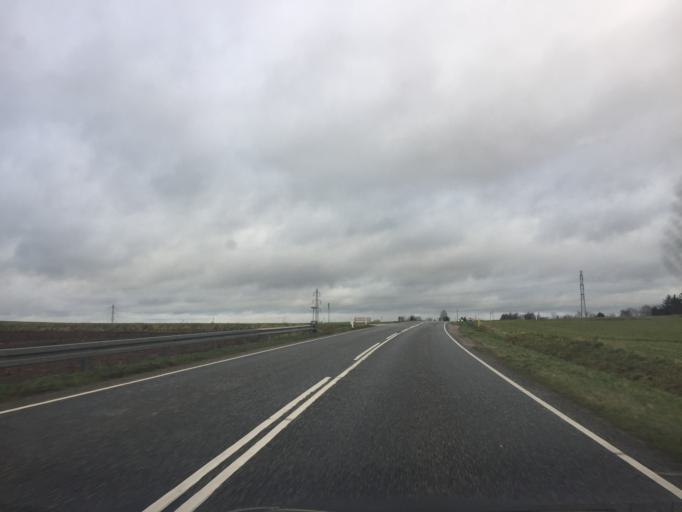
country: DK
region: Zealand
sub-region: Soro Kommune
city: Stenlille
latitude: 55.4914
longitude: 11.5743
